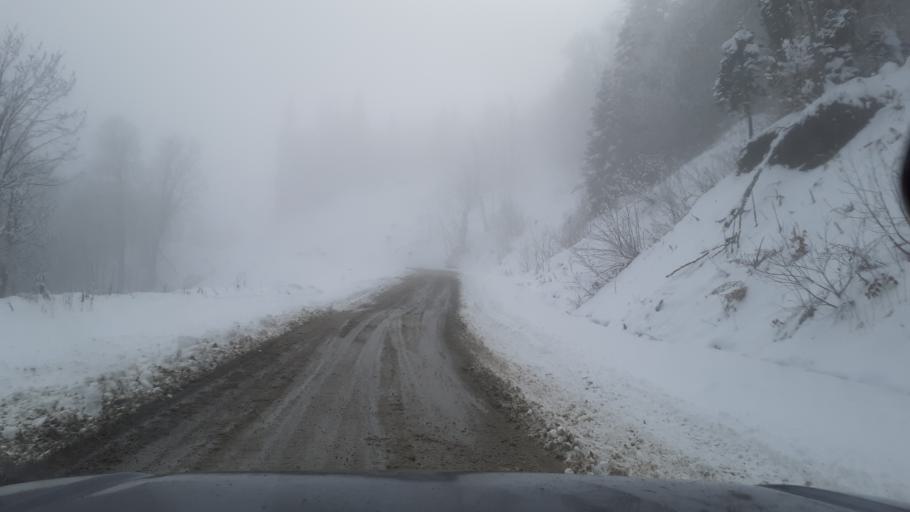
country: RU
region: Adygeya
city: Kamennomostskiy
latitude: 44.0089
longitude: 40.0231
